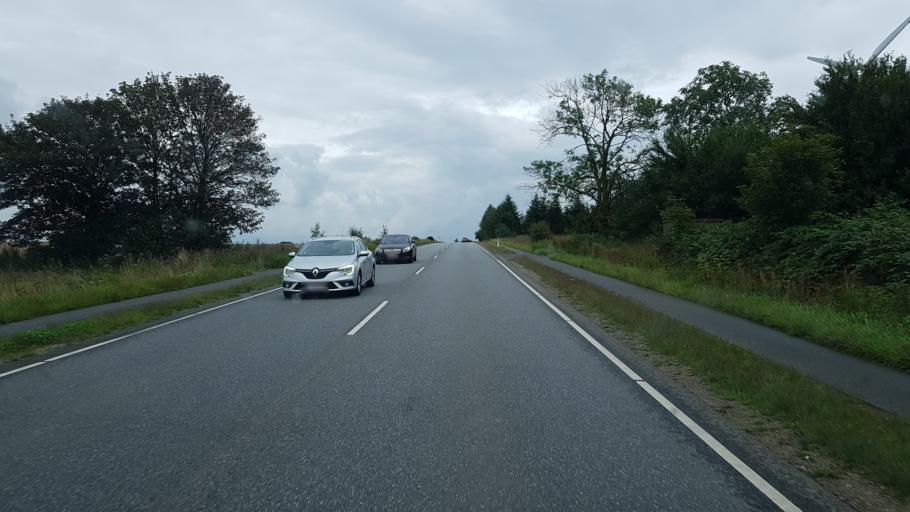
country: DK
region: Central Jutland
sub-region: Horsens Kommune
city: Braedstrup
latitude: 55.9160
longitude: 9.7021
